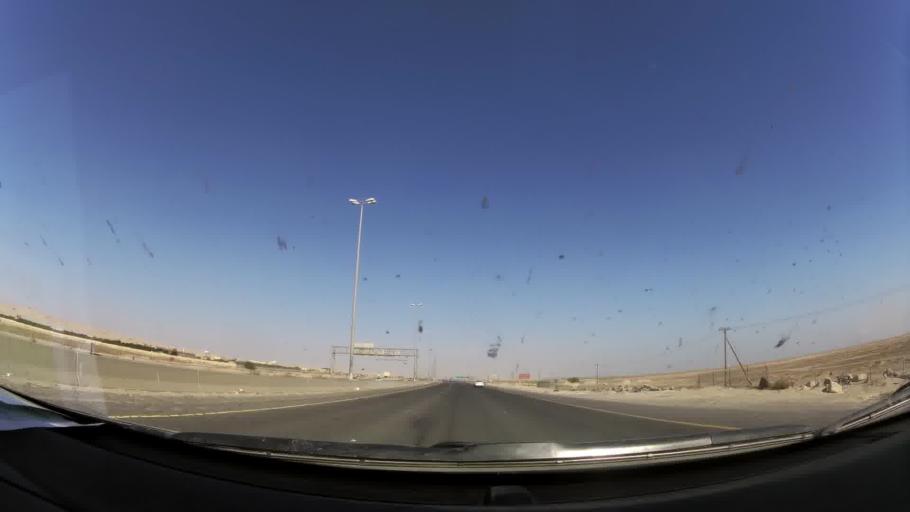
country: KW
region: Muhafazat al Jahra'
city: Al Jahra'
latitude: 29.3801
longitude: 47.6702
